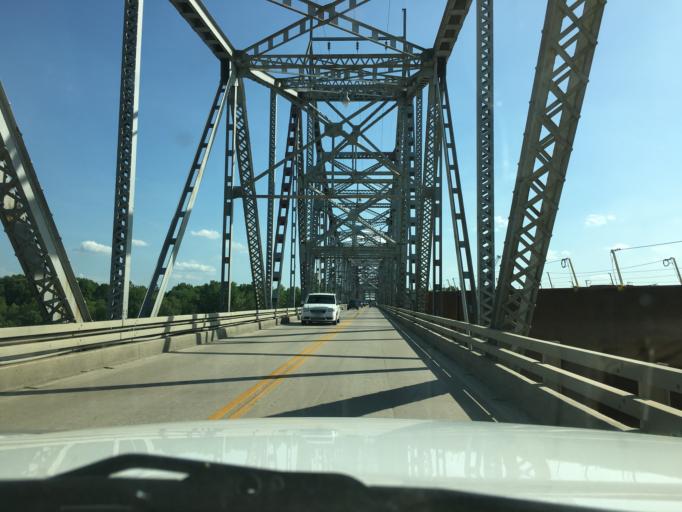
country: US
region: Missouri
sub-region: Franklin County
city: Washington
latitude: 38.5590
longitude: -90.9972
